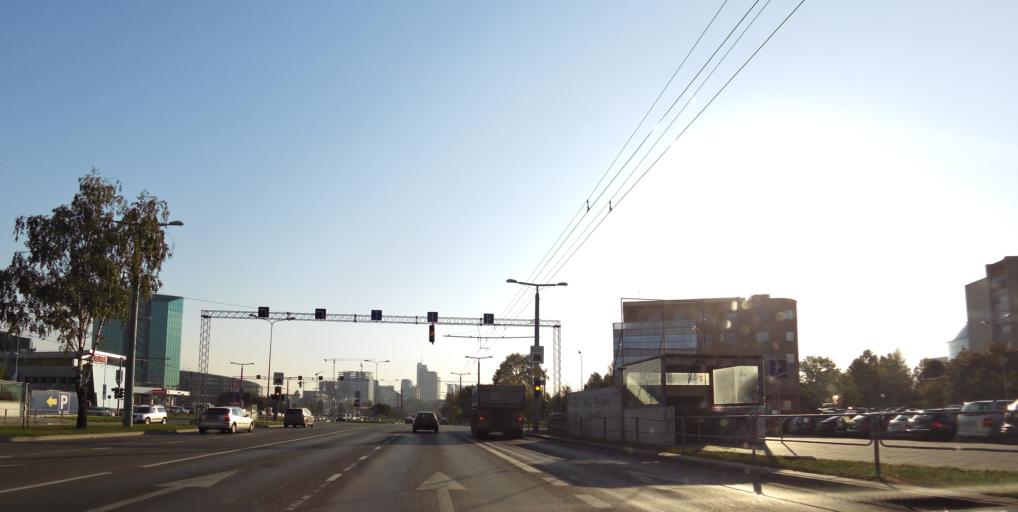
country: LT
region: Vilnius County
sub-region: Vilnius
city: Fabijoniskes
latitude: 54.7370
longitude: 25.2638
